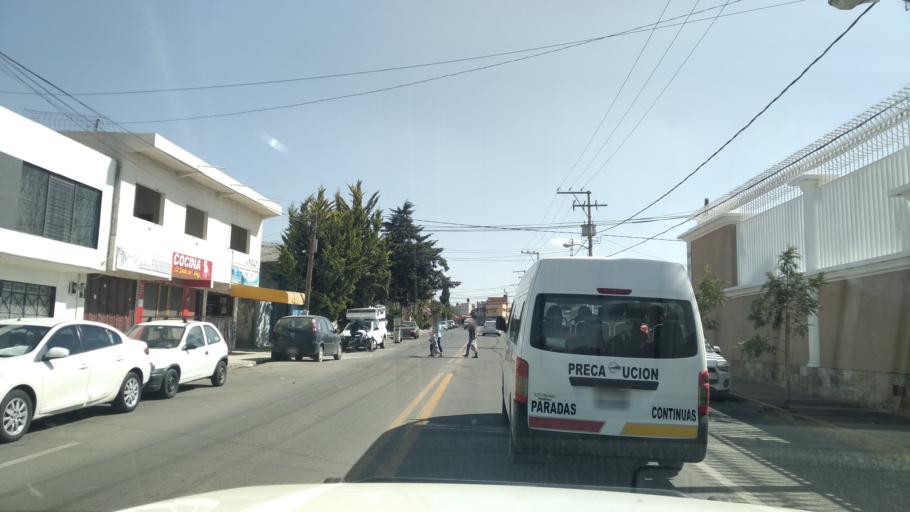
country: MX
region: Hidalgo
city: Calpulalpan
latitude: 19.5914
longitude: -98.5775
